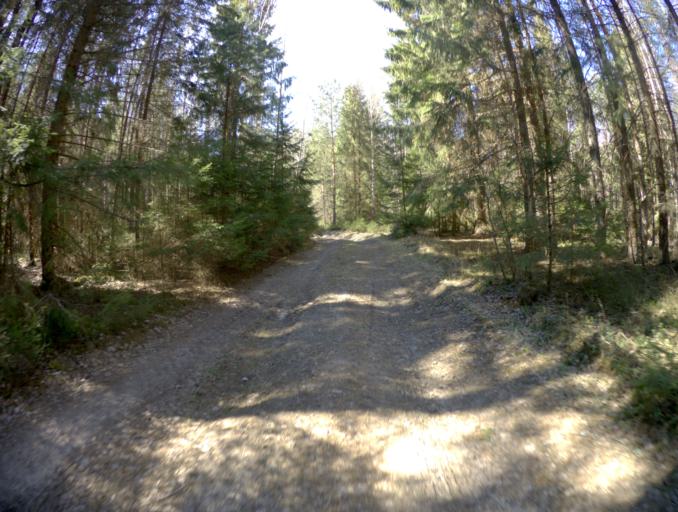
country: RU
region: Vladimir
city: Ivanishchi
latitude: 55.8399
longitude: 40.4388
